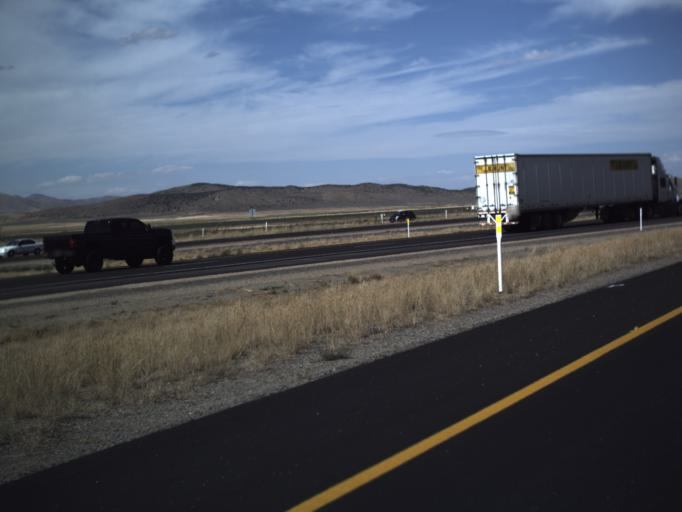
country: US
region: Utah
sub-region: Sanpete County
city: Gunnison
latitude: 39.2537
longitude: -112.1127
